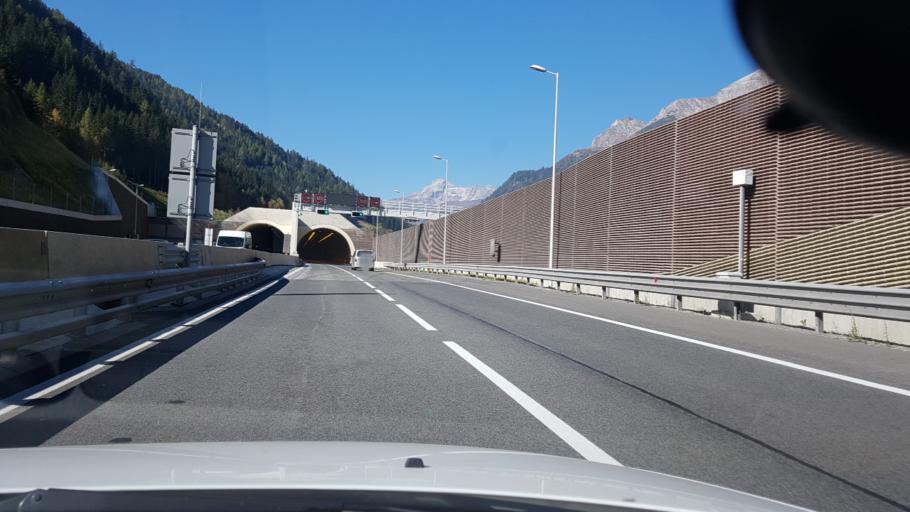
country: AT
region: Salzburg
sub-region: Politischer Bezirk Tamsweg
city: Zederhaus
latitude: 47.1472
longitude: 13.5173
